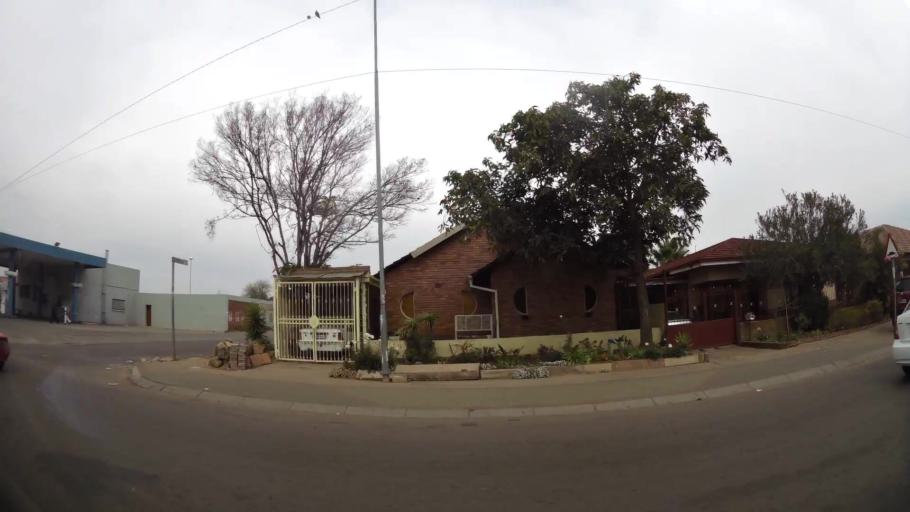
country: ZA
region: Gauteng
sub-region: City of Tshwane Metropolitan Municipality
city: Pretoria
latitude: -25.7110
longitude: 28.3457
